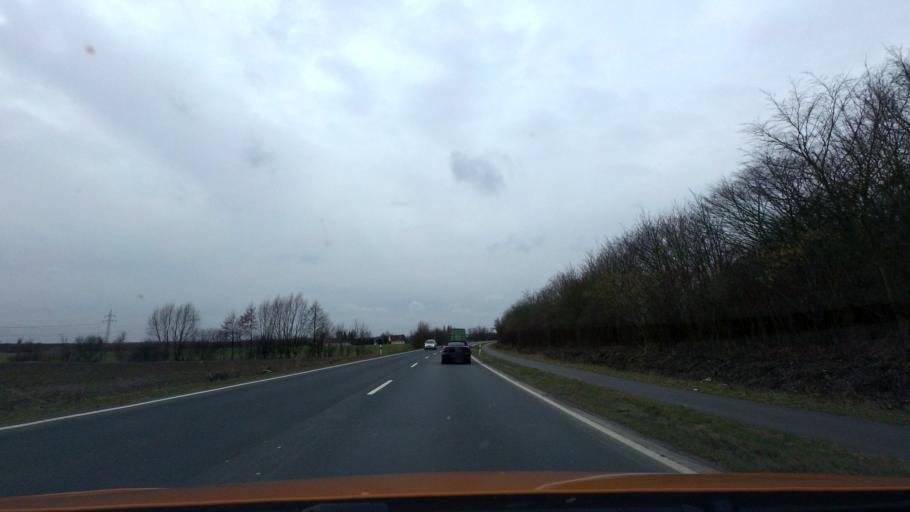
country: DE
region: Lower Saxony
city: Cremlingen
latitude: 52.2511
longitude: 10.6034
